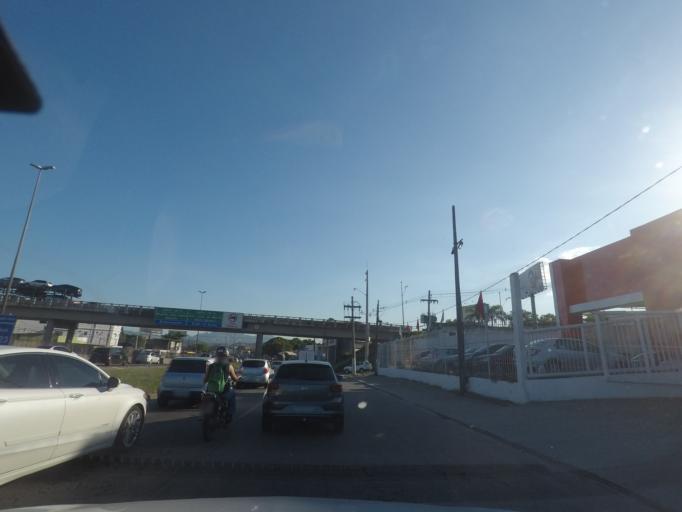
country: BR
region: Rio de Janeiro
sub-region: Duque De Caxias
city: Duque de Caxias
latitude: -22.7996
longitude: -43.2905
